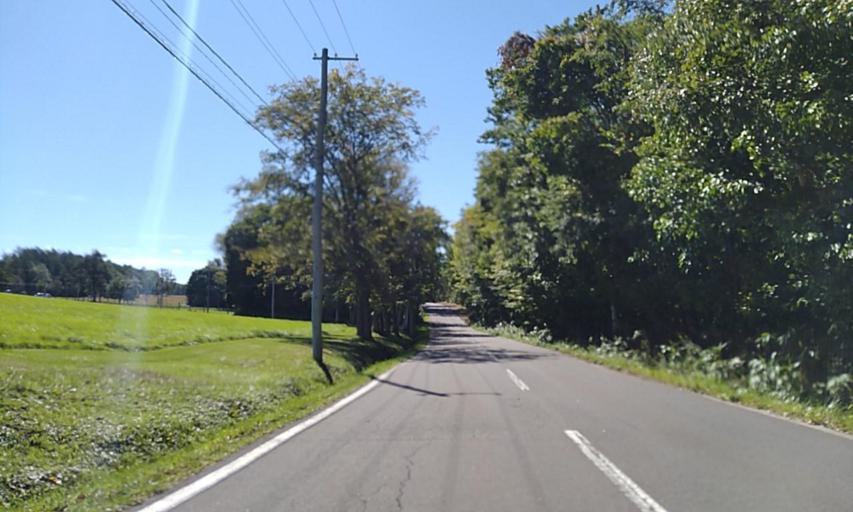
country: JP
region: Hokkaido
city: Sapporo
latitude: 43.0004
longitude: 141.3925
